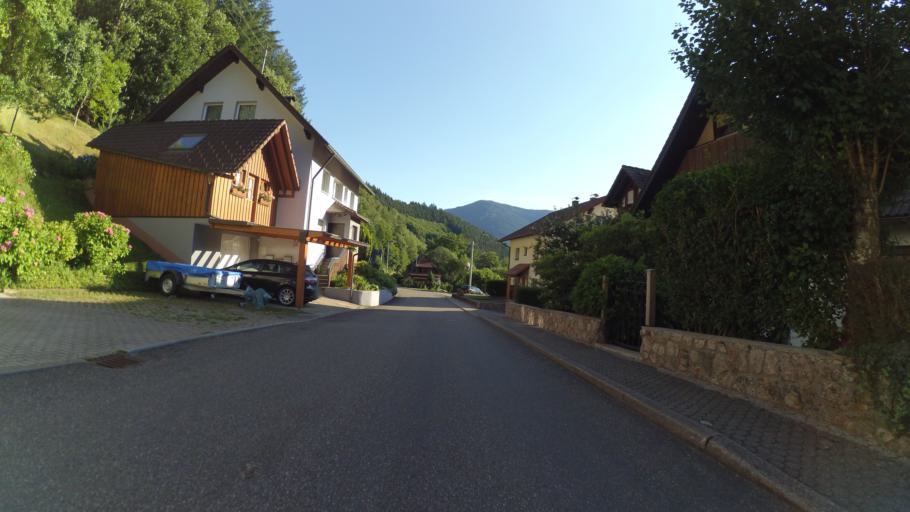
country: DE
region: Baden-Wuerttemberg
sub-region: Freiburg Region
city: Elzach
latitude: 48.1082
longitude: 8.0722
